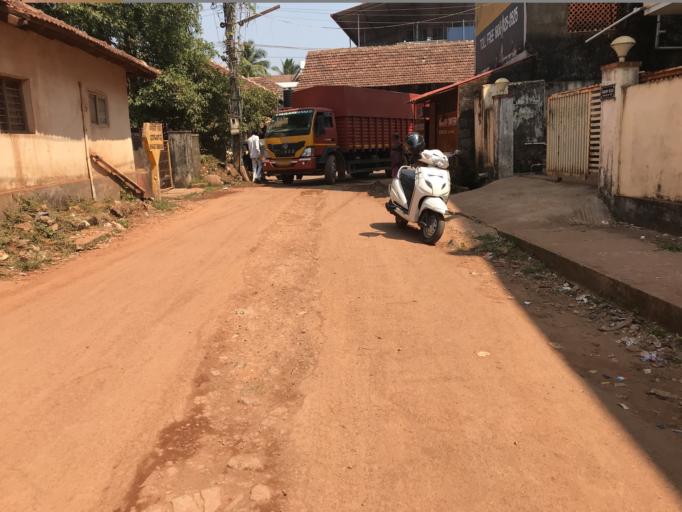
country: IN
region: Karnataka
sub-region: Dakshina Kannada
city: Ullal
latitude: 12.8509
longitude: 74.8369
